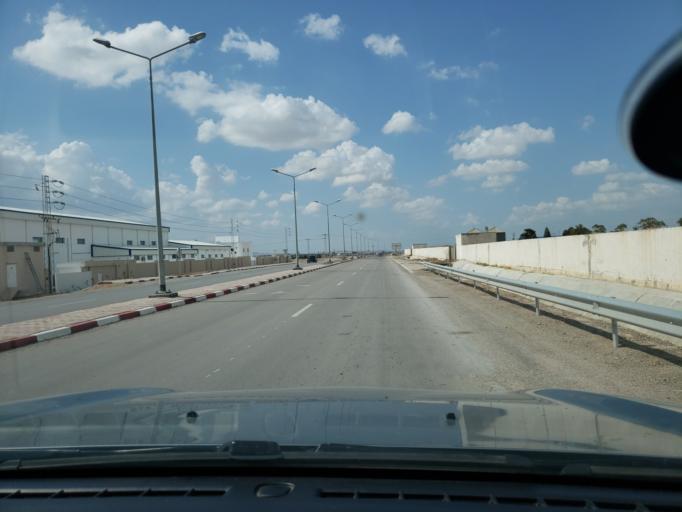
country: TN
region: Tunis
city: La Mohammedia
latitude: 36.5613
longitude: 10.0848
